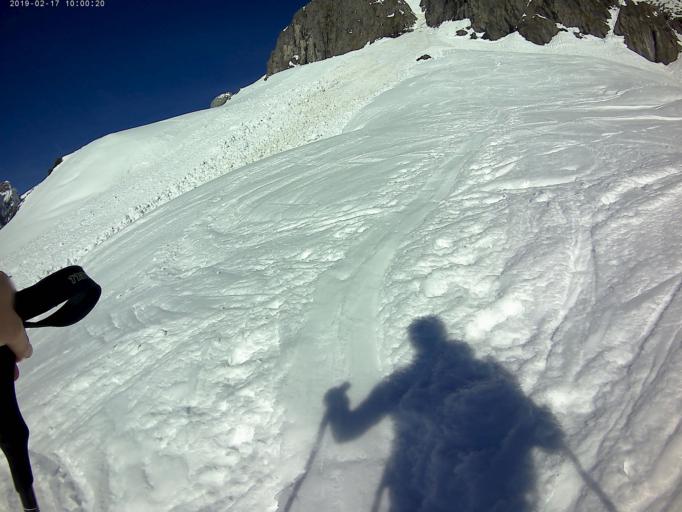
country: AT
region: Salzburg
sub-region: Politischer Bezirk Sankt Johann im Pongau
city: Muhlbach am Hochkonig
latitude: 47.4084
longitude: 13.0804
